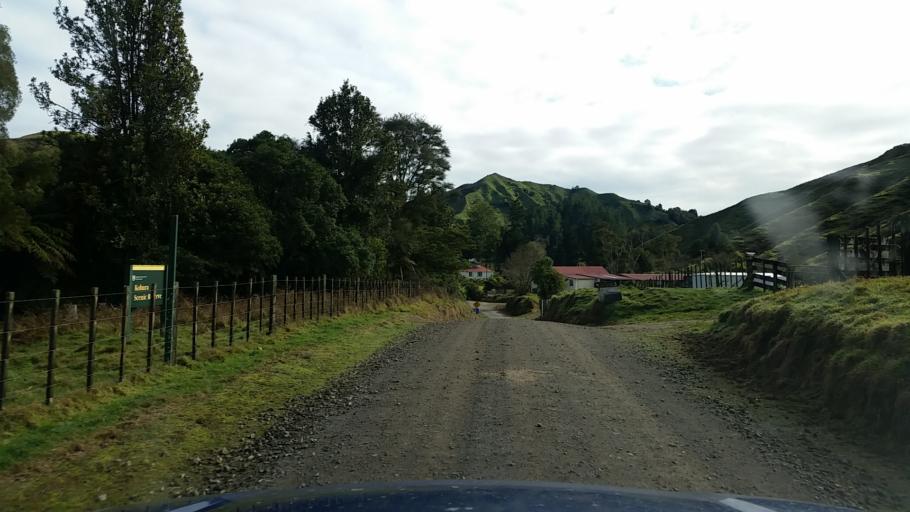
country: NZ
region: Taranaki
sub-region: New Plymouth District
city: Waitara
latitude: -39.1034
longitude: 174.8436
